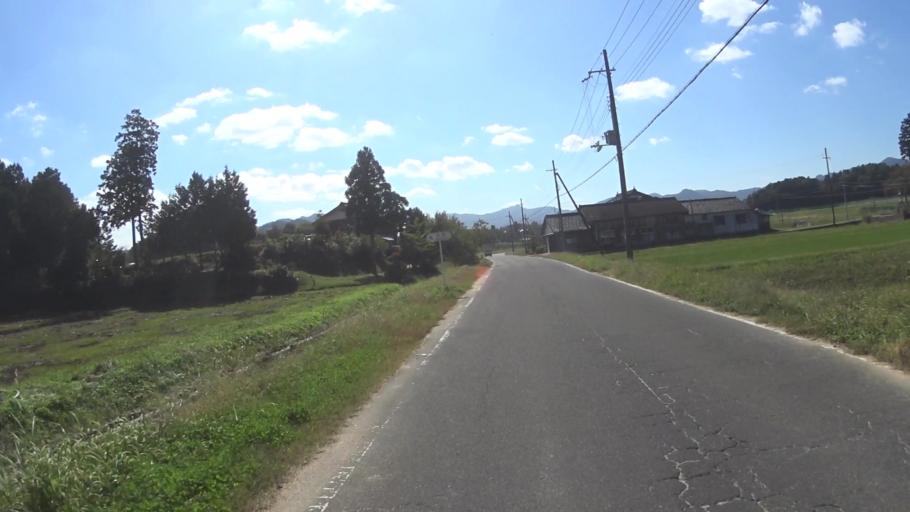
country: JP
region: Hyogo
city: Toyooka
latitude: 35.5935
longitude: 134.9451
